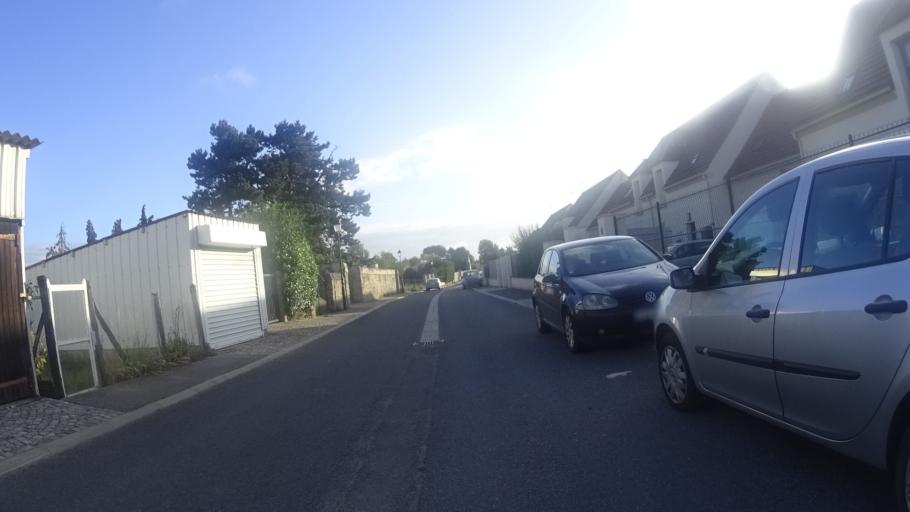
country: FR
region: Picardie
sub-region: Departement de l'Oise
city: Pontpoint
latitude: 49.2729
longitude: 2.6877
